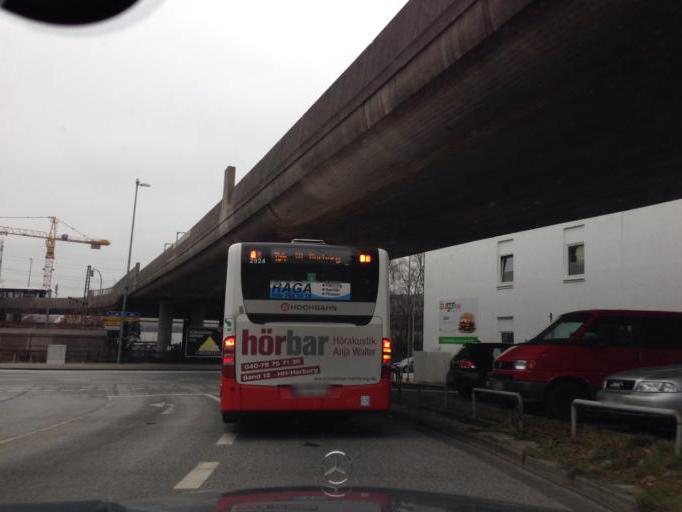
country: DE
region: Hamburg
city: Harburg
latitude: 53.4644
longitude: 9.9779
